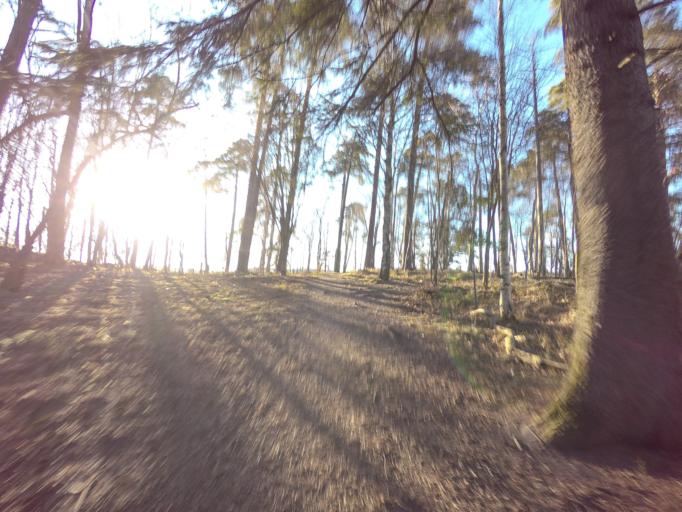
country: FI
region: Uusimaa
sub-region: Helsinki
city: Helsinki
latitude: 60.1833
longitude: 25.0360
